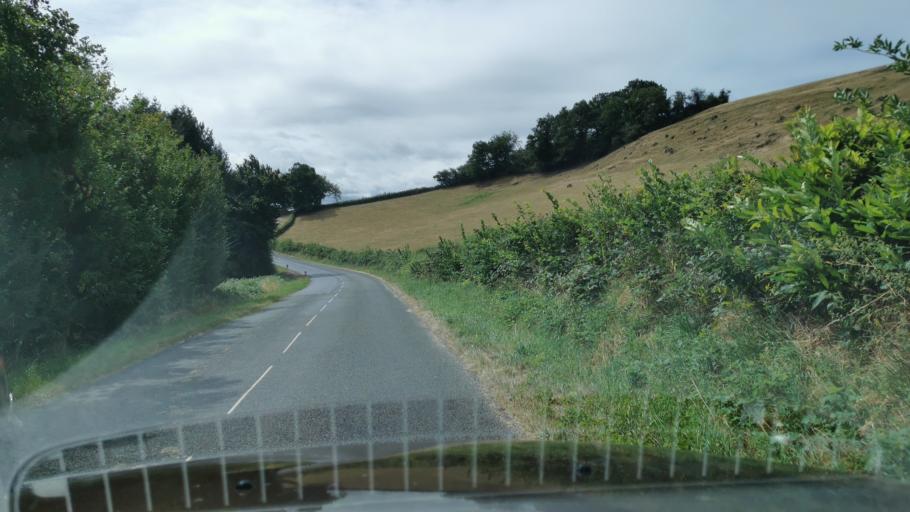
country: FR
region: Bourgogne
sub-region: Departement de Saone-et-Loire
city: Montcenis
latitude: 46.8016
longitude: 4.3588
